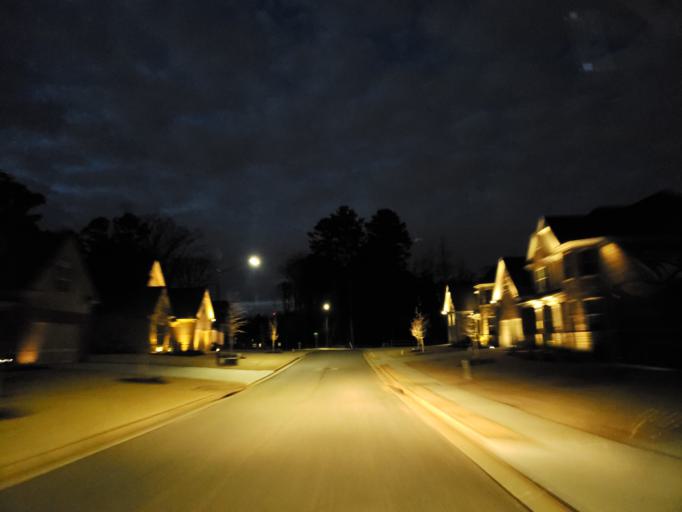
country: US
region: Georgia
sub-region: Cobb County
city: Kennesaw
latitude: 33.9847
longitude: -84.6282
